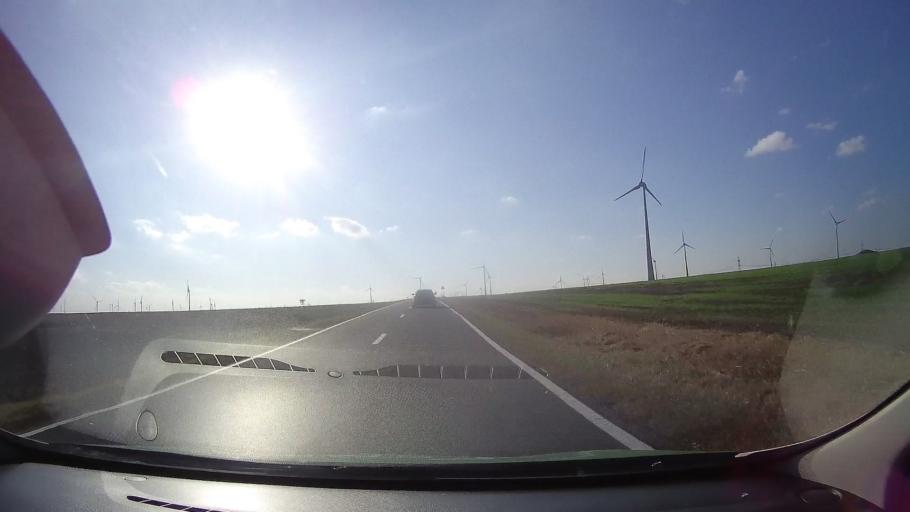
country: RO
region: Tulcea
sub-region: Comuna Topolog
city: Topolog
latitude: 44.8206
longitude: 28.2638
